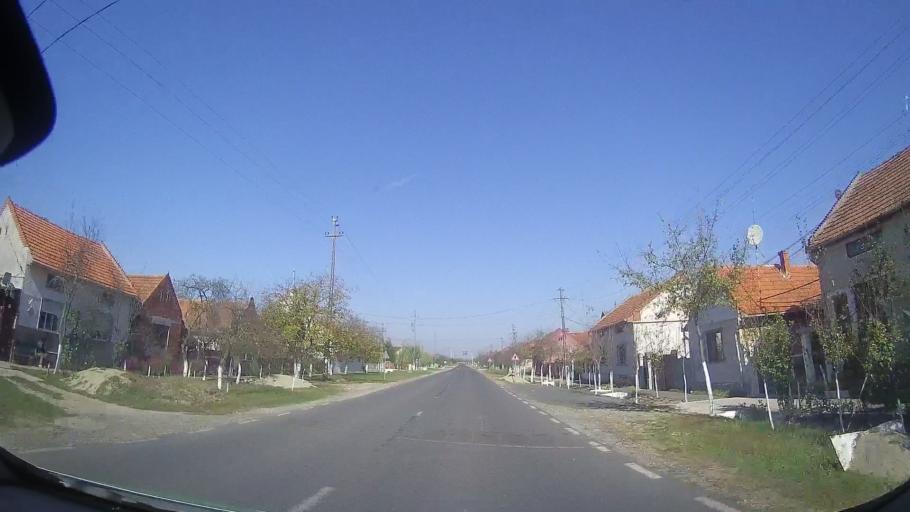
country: RO
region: Timis
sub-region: Comuna Costeiu
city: Costeiu
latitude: 45.7756
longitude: 21.8492
